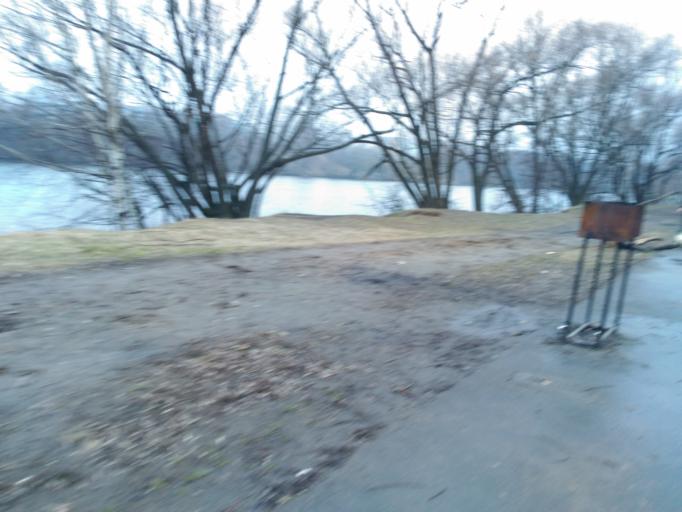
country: RU
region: Moscow
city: Shchukino
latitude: 55.7753
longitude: 37.4294
